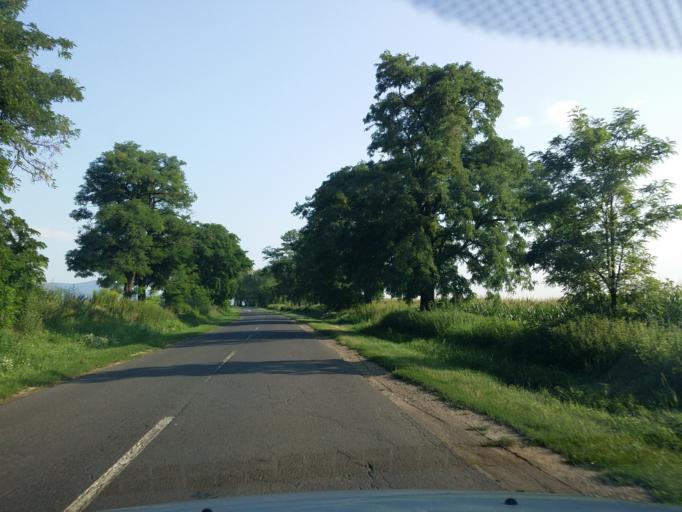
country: HU
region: Borsod-Abauj-Zemplen
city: Gonc
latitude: 48.4386
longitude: 21.2381
